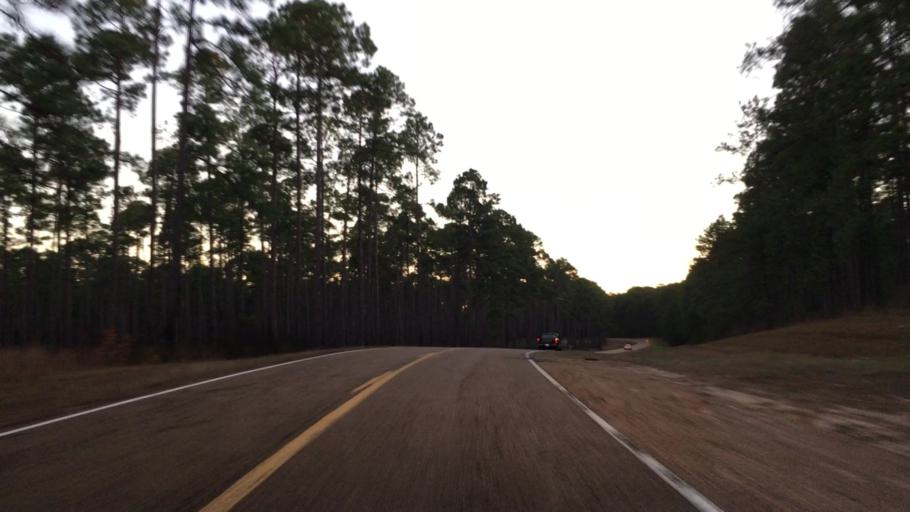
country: US
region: Louisiana
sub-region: Vernon Parish
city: Fort Polk South
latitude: 31.0226
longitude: -93.1891
